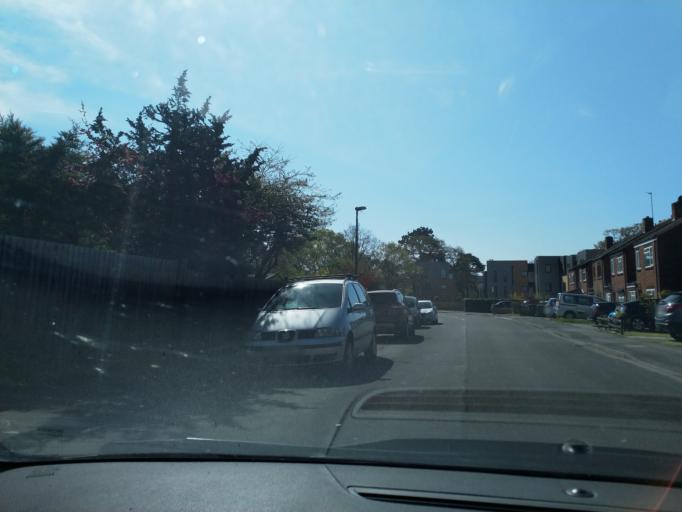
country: GB
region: England
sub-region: Oxfordshire
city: Cowley
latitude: 51.7469
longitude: -1.2023
